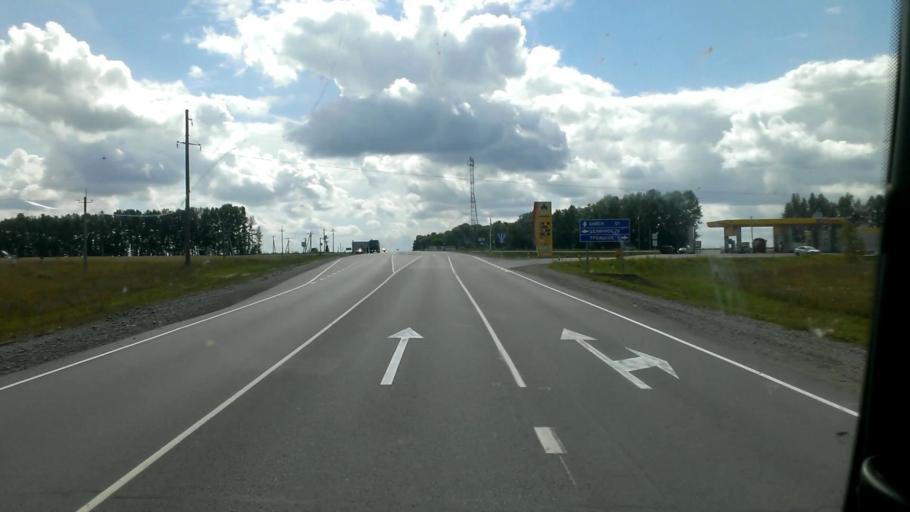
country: RU
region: Altai Krai
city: Troitskoye
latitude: 52.9692
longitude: 84.7494
